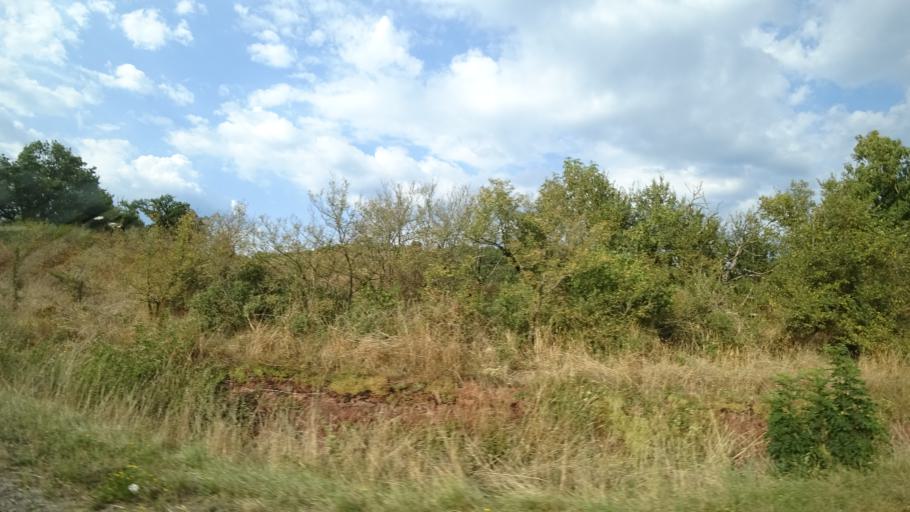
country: FR
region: Midi-Pyrenees
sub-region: Departement de l'Aveyron
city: Saint-Christophe-Vallon
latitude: 44.4864
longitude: 2.3959
